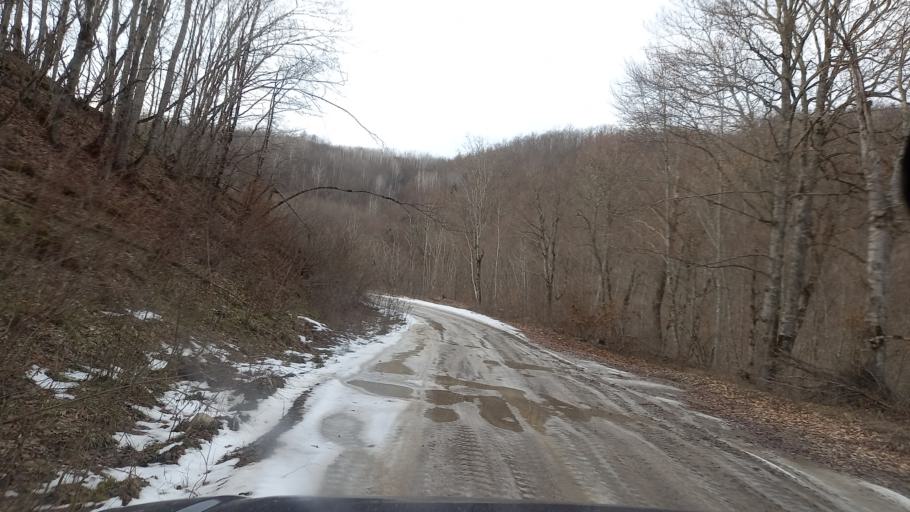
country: RU
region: Adygeya
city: Kamennomostskiy
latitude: 44.1513
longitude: 40.2964
